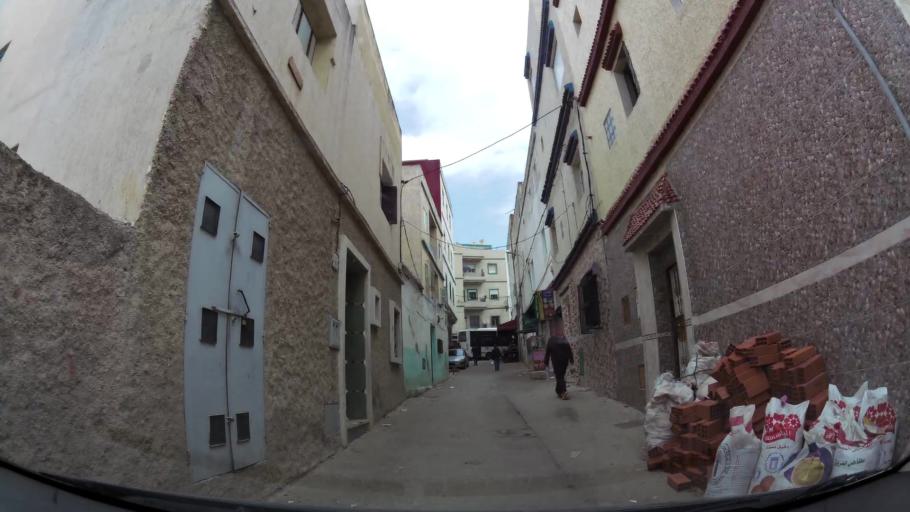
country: MA
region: Tanger-Tetouan
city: Tetouan
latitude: 35.5661
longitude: -5.3950
